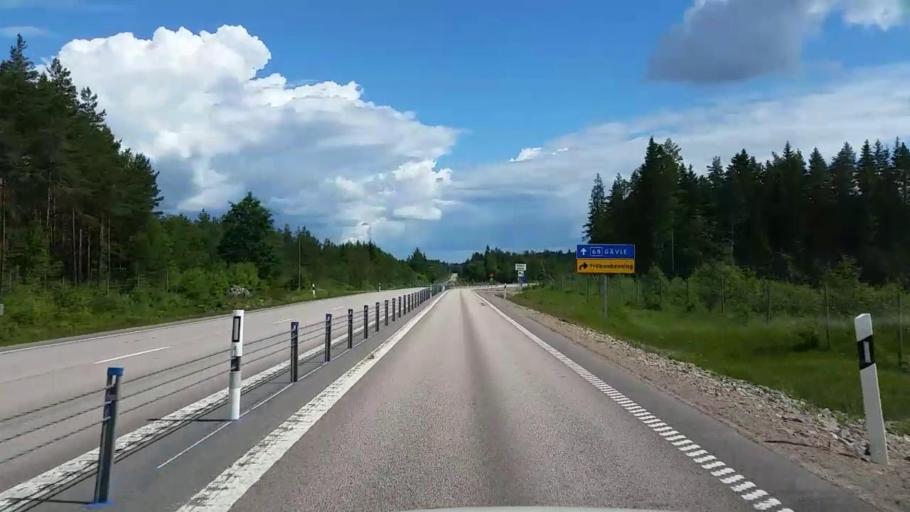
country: SE
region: Dalarna
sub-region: Avesta Kommun
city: Avesta
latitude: 60.1221
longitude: 16.0919
